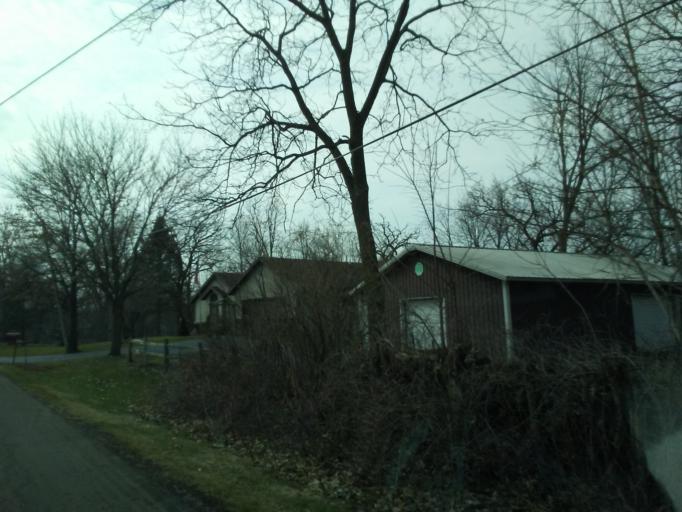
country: US
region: Wisconsin
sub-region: Columbia County
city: Lodi
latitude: 43.3241
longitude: -89.5316
